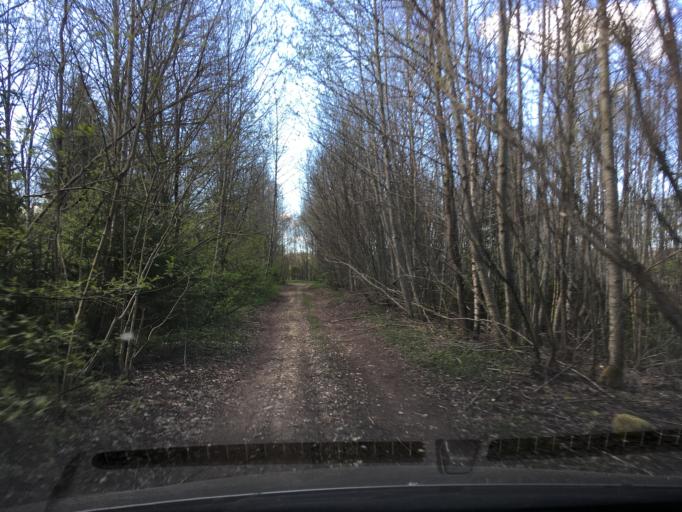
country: EE
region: Harju
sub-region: Raasiku vald
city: Raasiku
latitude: 59.2061
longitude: 25.1370
